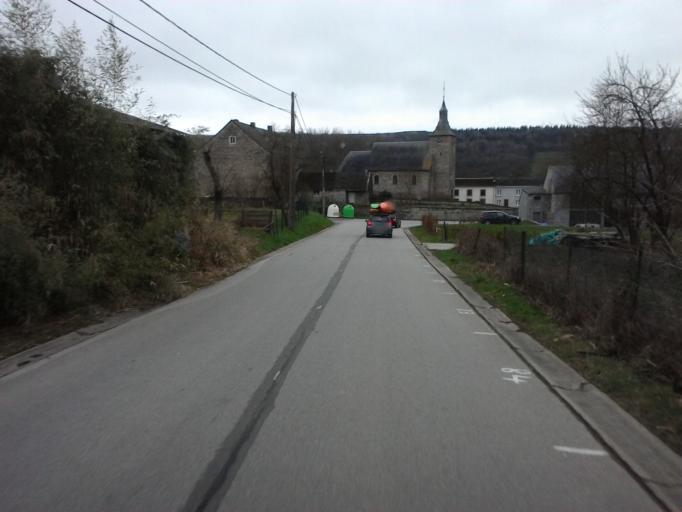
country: BE
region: Wallonia
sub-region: Province du Luxembourg
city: Wellin
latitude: 50.1096
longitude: 5.1419
